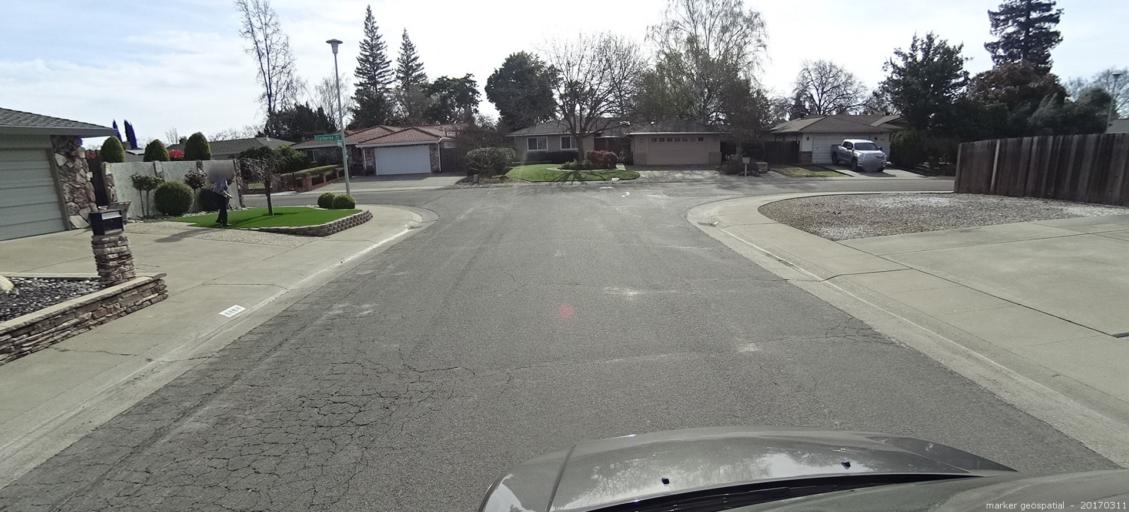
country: US
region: California
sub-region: Yolo County
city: West Sacramento
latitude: 38.5019
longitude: -121.5501
